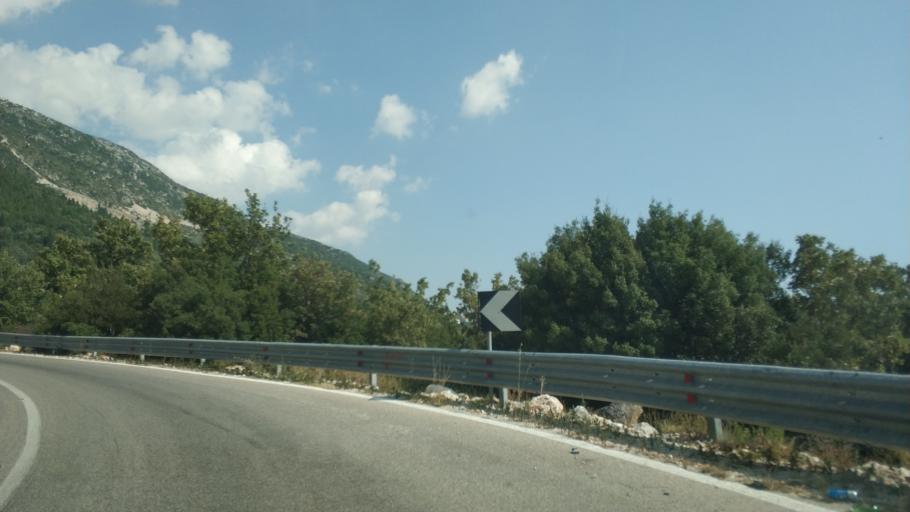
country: AL
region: Vlore
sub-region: Rrethi i Vlores
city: Vranisht
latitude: 40.1740
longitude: 19.6072
